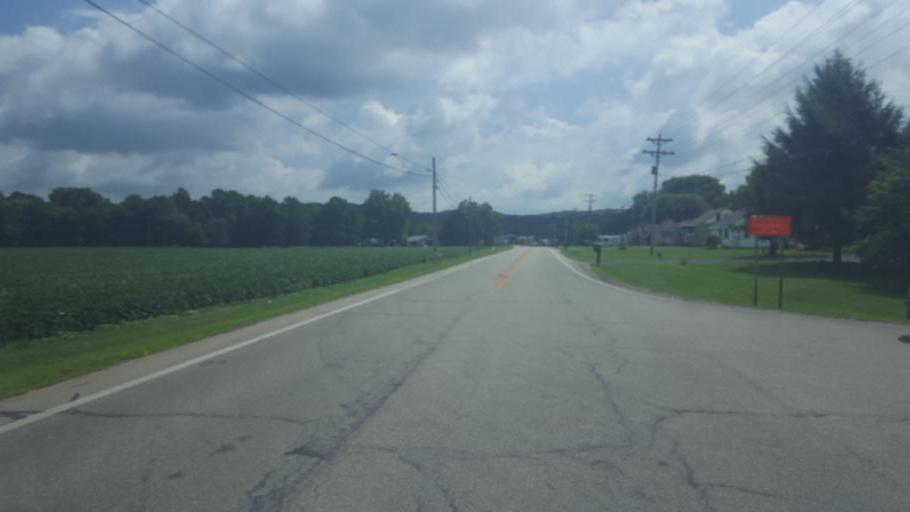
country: US
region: Ohio
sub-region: Ross County
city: Kingston
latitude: 39.4752
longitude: -82.7510
